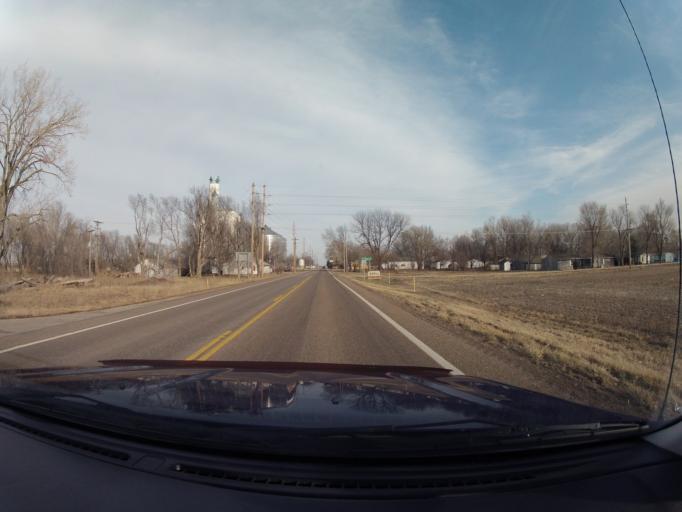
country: US
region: Kansas
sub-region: Pottawatomie County
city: Saint Marys
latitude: 39.2158
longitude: -96.1839
